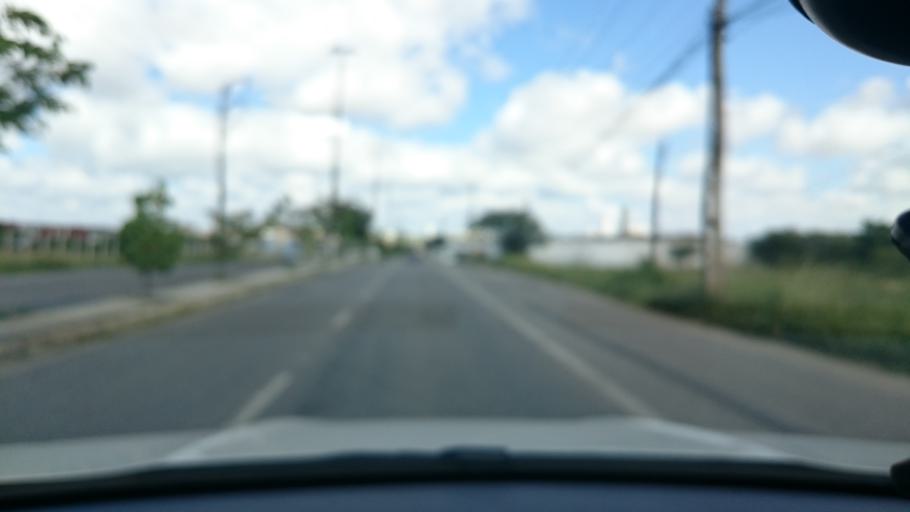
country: BR
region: Paraiba
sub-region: Campina Grande
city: Campina Grande
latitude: -7.2334
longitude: -35.9146
